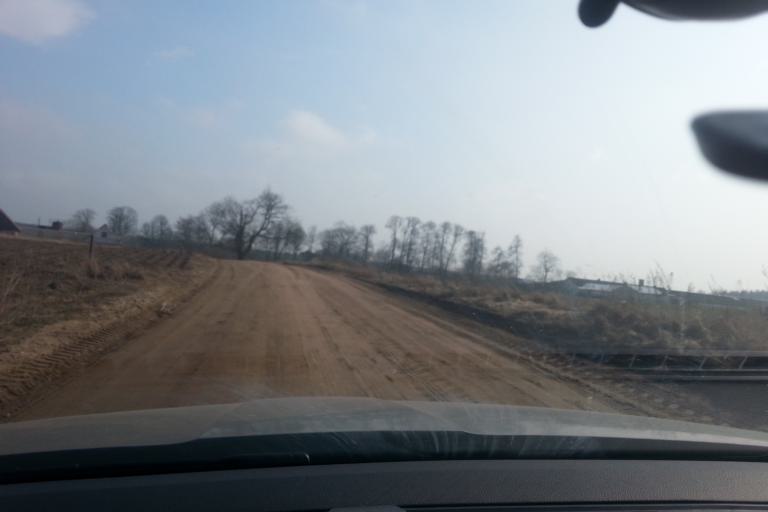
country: LT
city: Trakai
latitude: 54.4992
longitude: 24.9759
